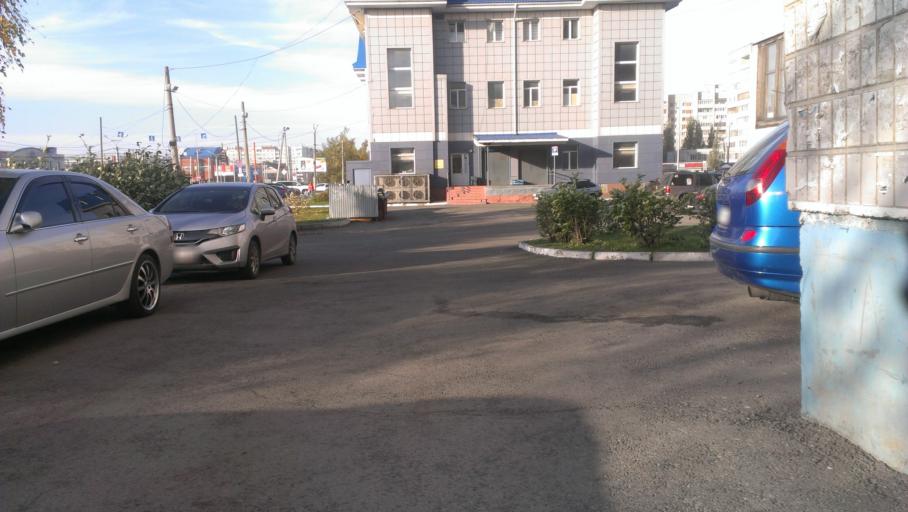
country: RU
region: Altai Krai
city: Novosilikatnyy
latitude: 53.3349
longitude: 83.6694
